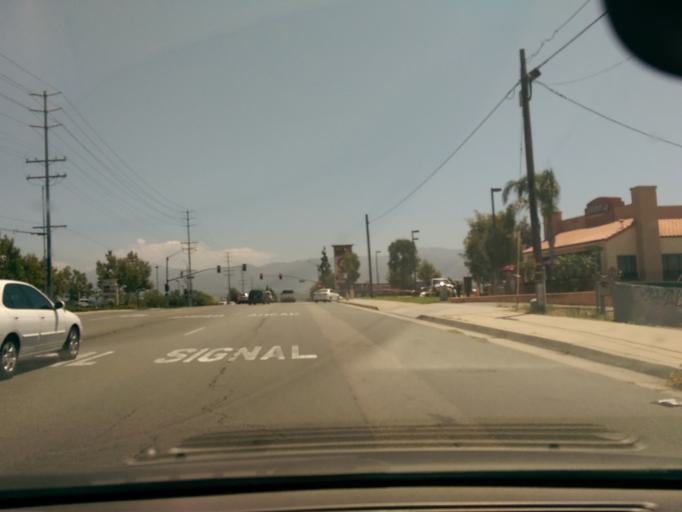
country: US
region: California
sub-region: Riverside County
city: Corona
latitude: 33.9034
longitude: -117.5622
